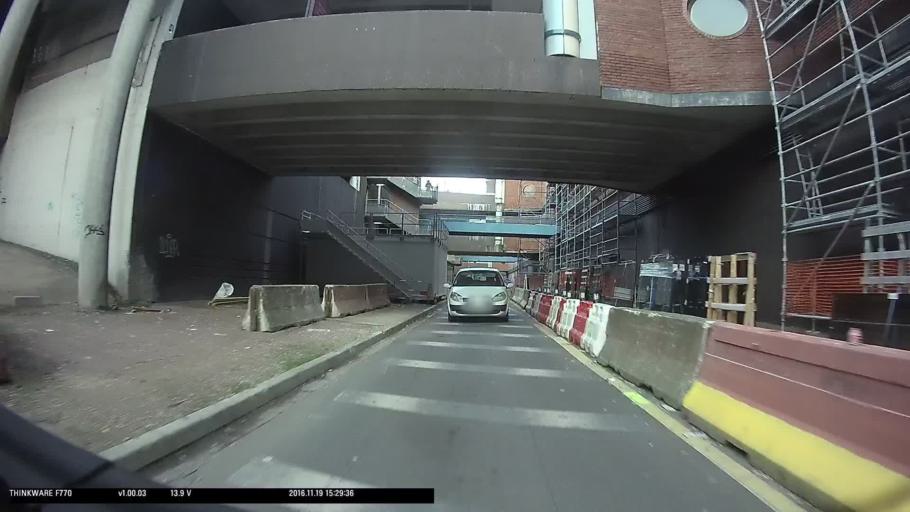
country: FR
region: Ile-de-France
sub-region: Departement du Val-d'Oise
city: Cergy-Pontoise
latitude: 49.0382
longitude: 2.0799
